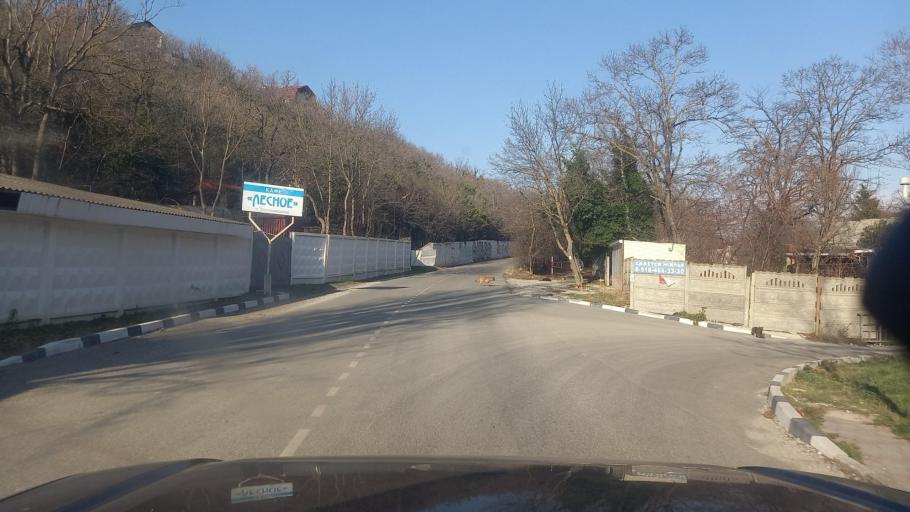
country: RU
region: Krasnodarskiy
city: Myskhako
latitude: 44.6627
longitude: 37.6849
